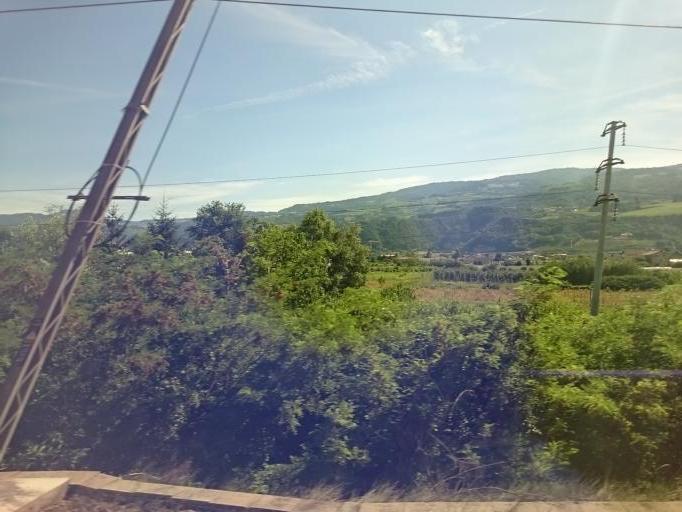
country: IT
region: Trentino-Alto Adige
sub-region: Provincia di Trento
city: Meano
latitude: 46.1130
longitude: 11.0937
